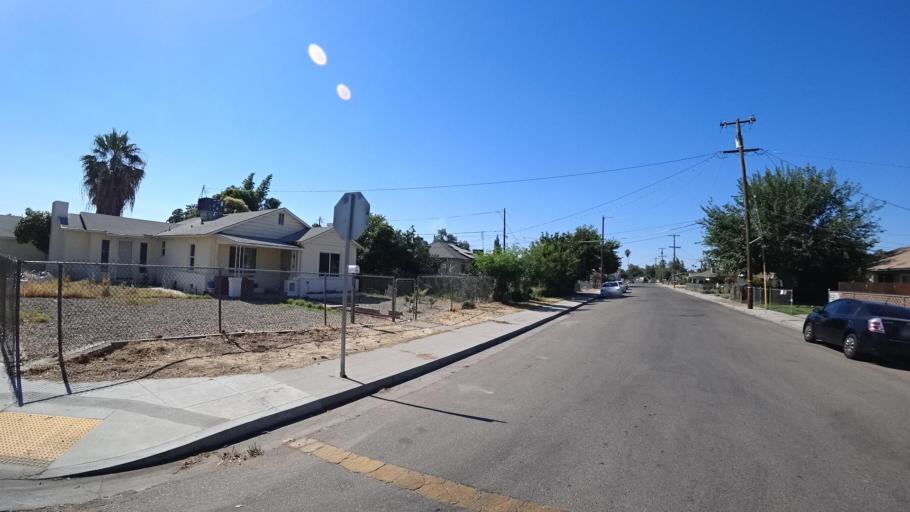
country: US
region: California
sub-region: Fresno County
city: Fresno
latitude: 36.7665
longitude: -119.8239
